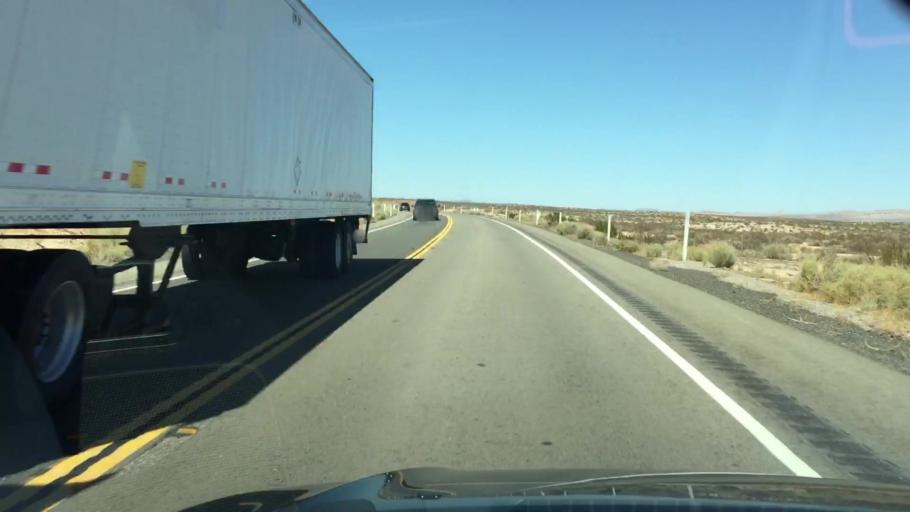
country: US
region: California
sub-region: Kern County
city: Boron
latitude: 35.0680
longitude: -117.5592
